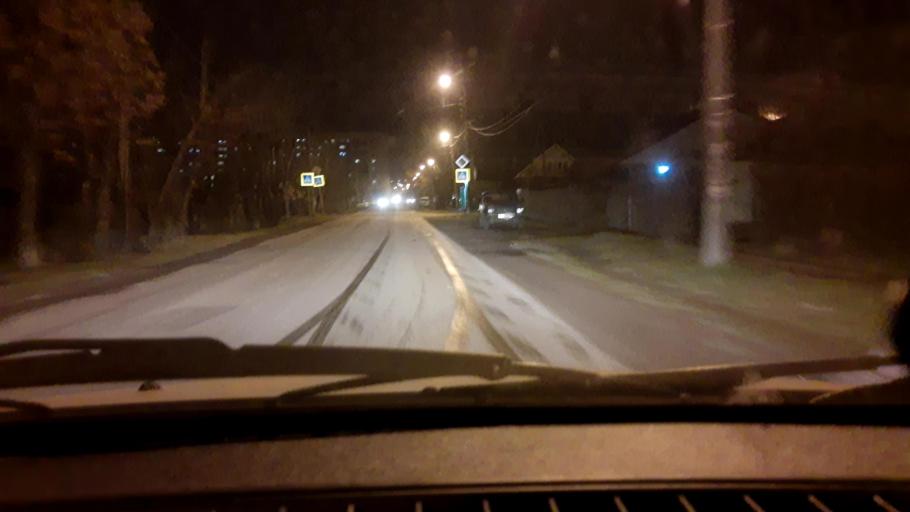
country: RU
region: Bashkortostan
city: Avdon
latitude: 54.7002
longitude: 55.8215
